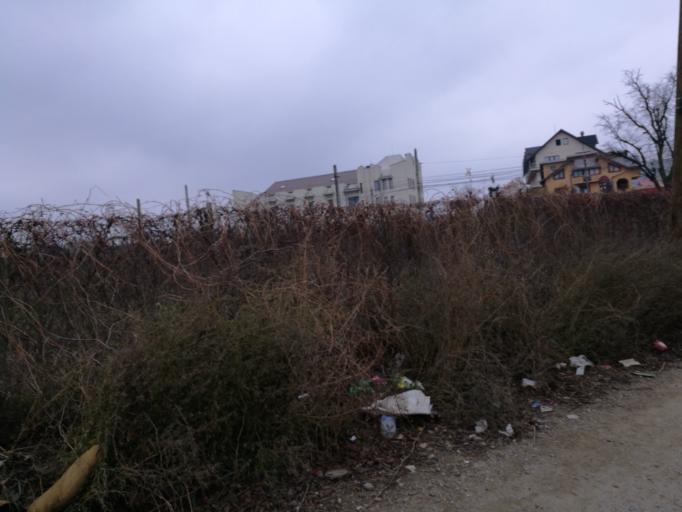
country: RO
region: Suceava
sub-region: Comuna Scheia
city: Scheia
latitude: 47.6739
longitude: 26.2715
